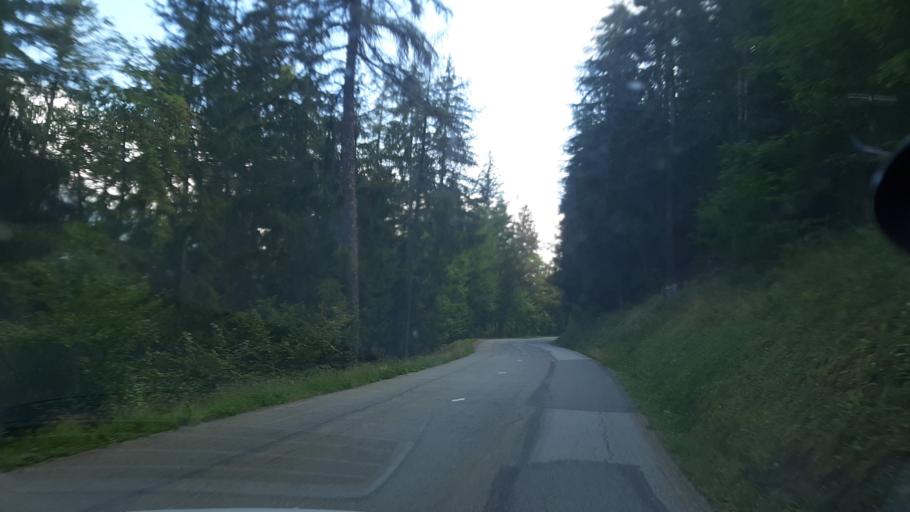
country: FR
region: Rhone-Alpes
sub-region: Departement de la Savoie
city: Aime
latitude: 45.5276
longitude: 6.6099
